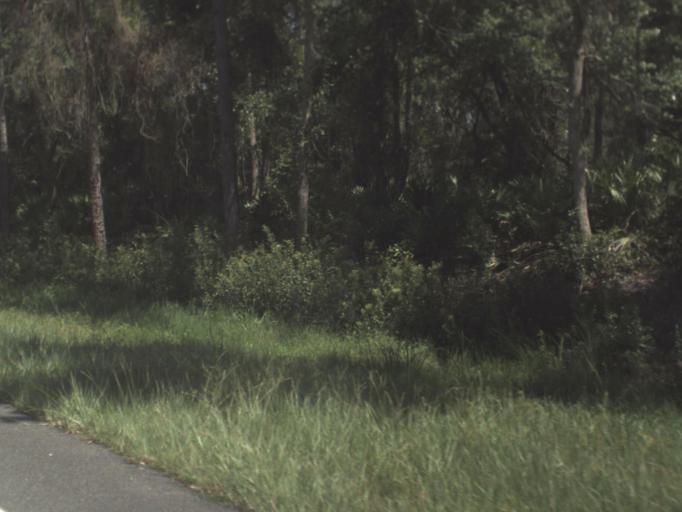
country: US
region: Florida
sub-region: Clay County
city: Green Cove Springs
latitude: 30.0149
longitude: -81.6263
